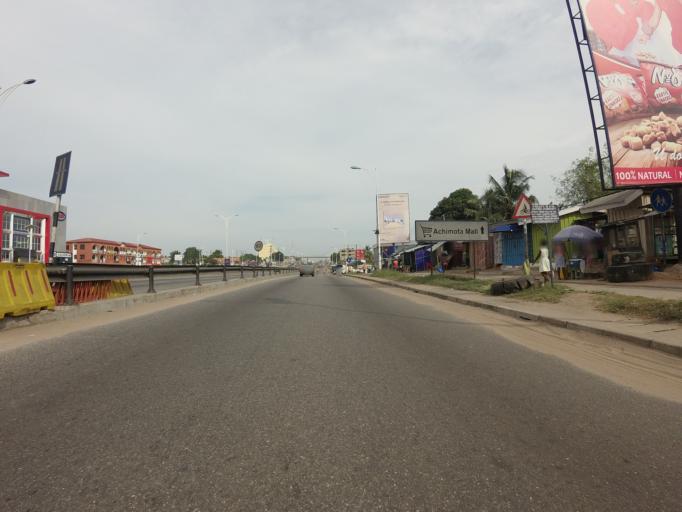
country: GH
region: Greater Accra
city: Dome
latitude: 5.6250
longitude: -0.2335
